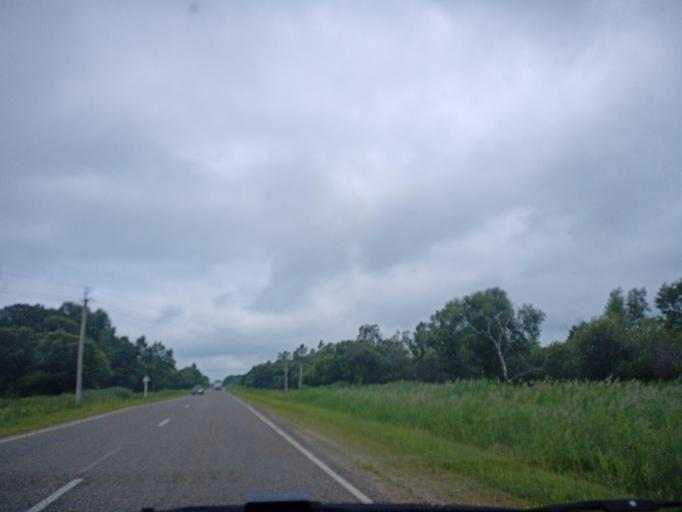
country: RU
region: Primorskiy
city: Novopokrovka
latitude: 45.9703
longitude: 134.2401
